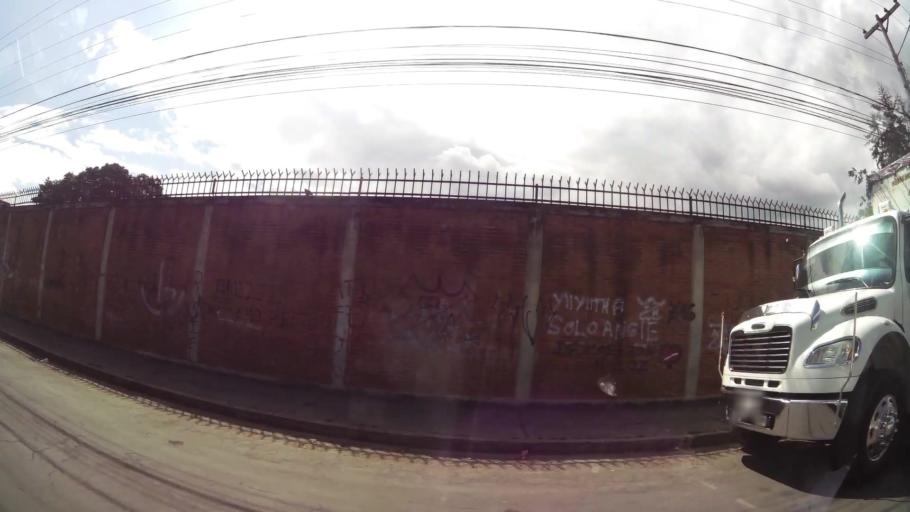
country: CO
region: Bogota D.C.
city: Bogota
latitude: 4.6339
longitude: -74.1178
